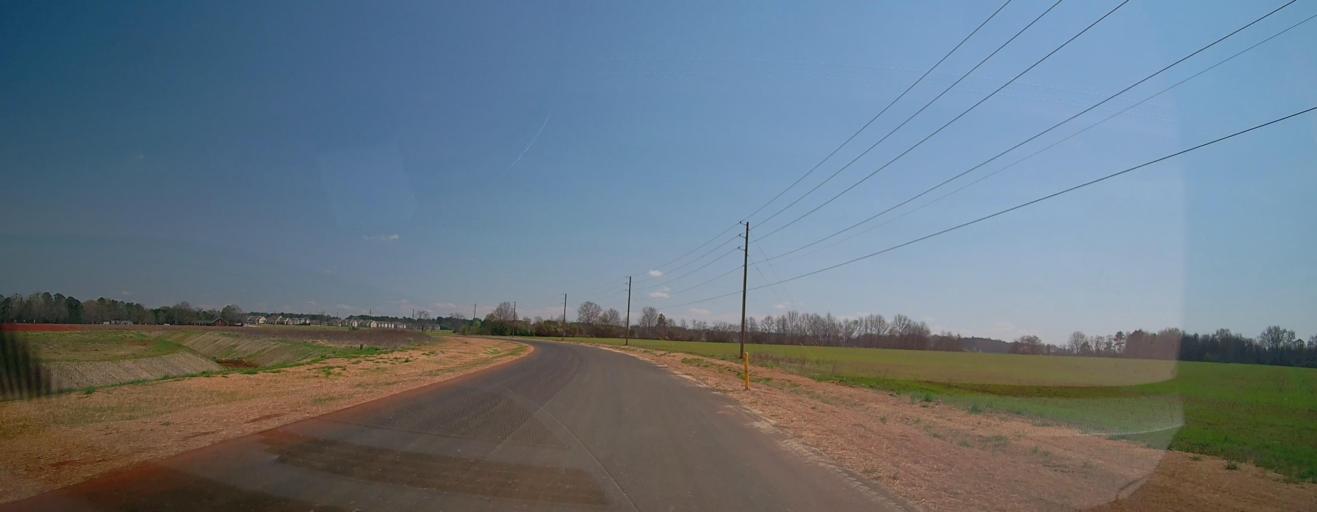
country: US
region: Georgia
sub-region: Houston County
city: Centerville
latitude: 32.5969
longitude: -83.7261
